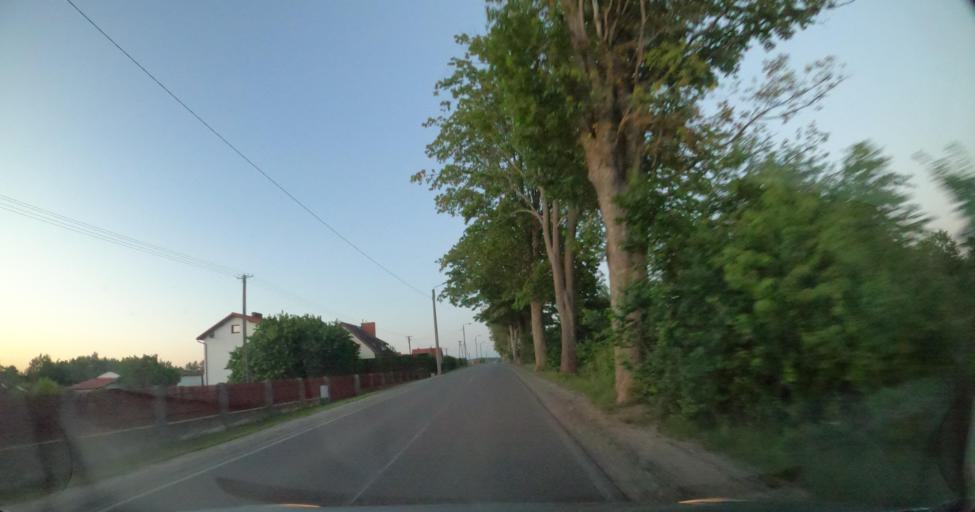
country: PL
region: Pomeranian Voivodeship
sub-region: Powiat wejherowski
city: Szemud
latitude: 54.4831
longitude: 18.2107
